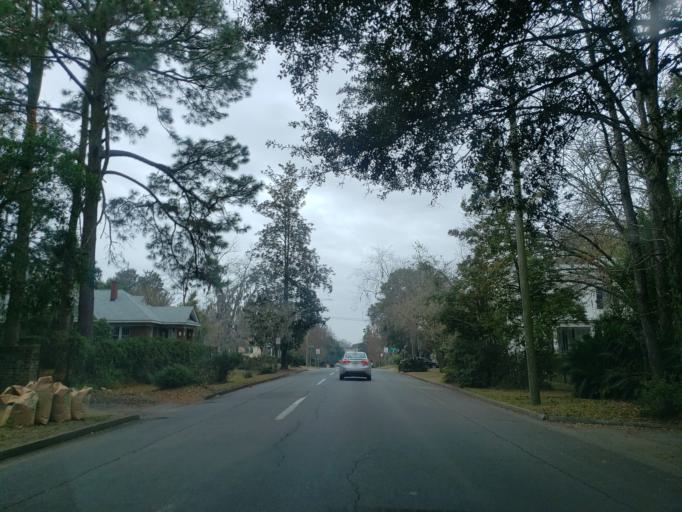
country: US
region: Georgia
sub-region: Chatham County
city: Thunderbolt
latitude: 32.0559
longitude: -81.0698
